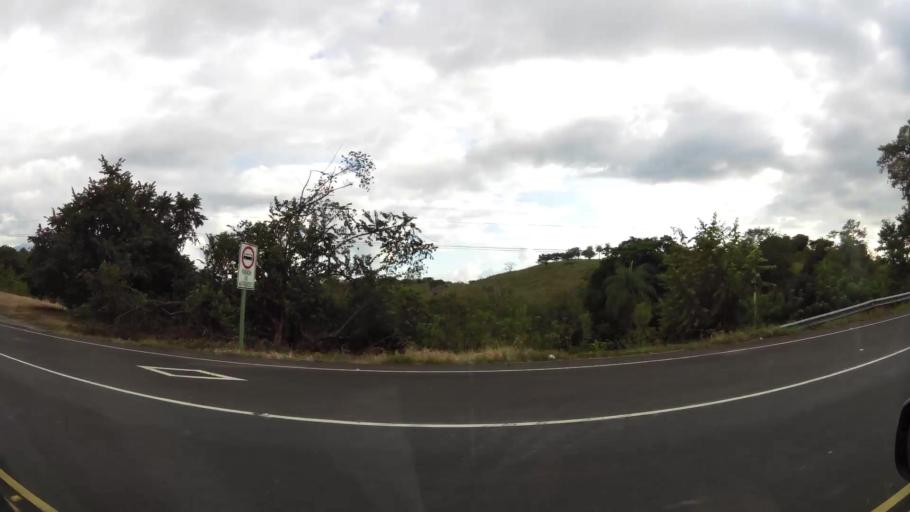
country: CR
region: Alajuela
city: Orotina
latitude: 9.8912
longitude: -84.6056
